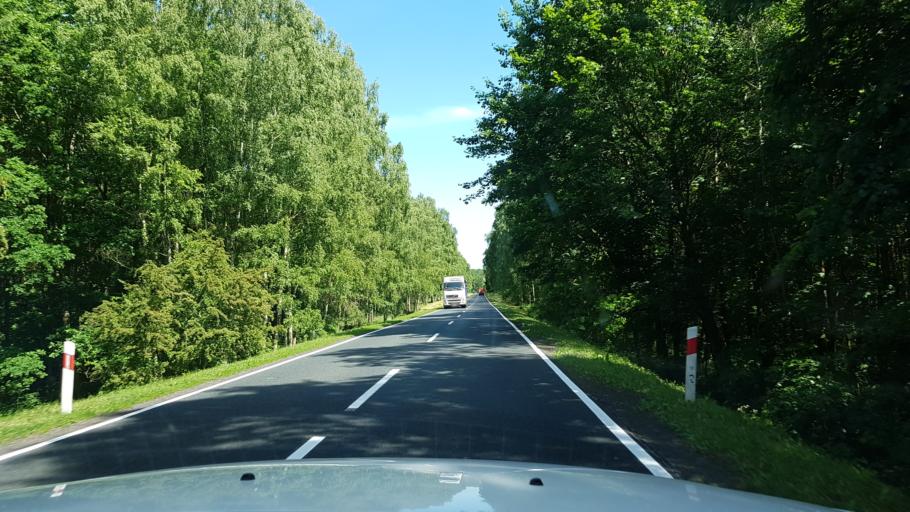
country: PL
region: West Pomeranian Voivodeship
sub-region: Powiat gryfinski
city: Chojna
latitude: 52.9614
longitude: 14.4911
